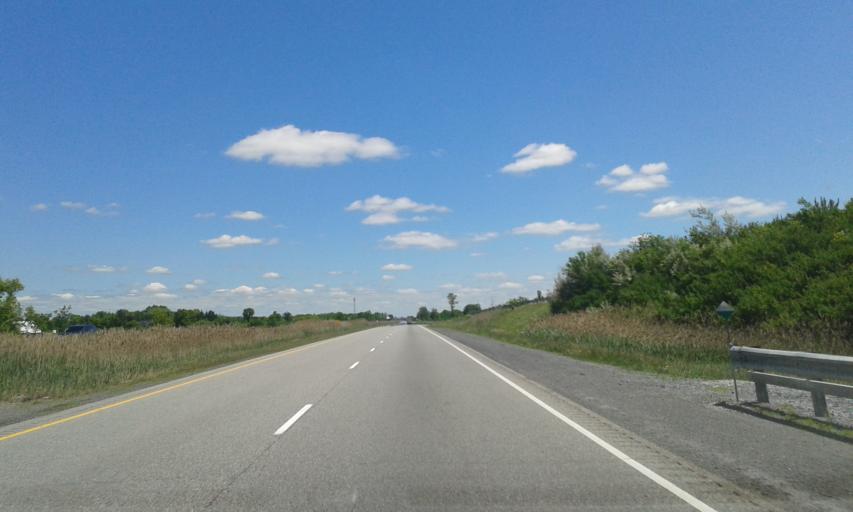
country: US
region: New York
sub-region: St. Lawrence County
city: Norfolk
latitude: 44.9530
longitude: -75.1102
